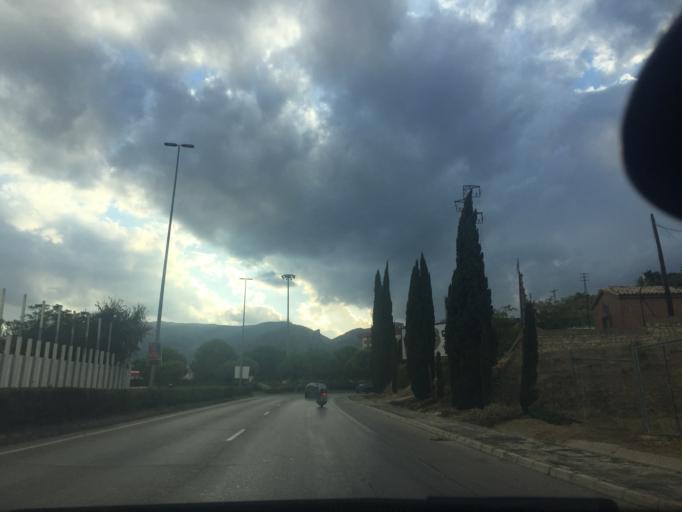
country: ES
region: Andalusia
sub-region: Provincia de Jaen
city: Jaen
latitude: 37.7706
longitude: -3.7765
